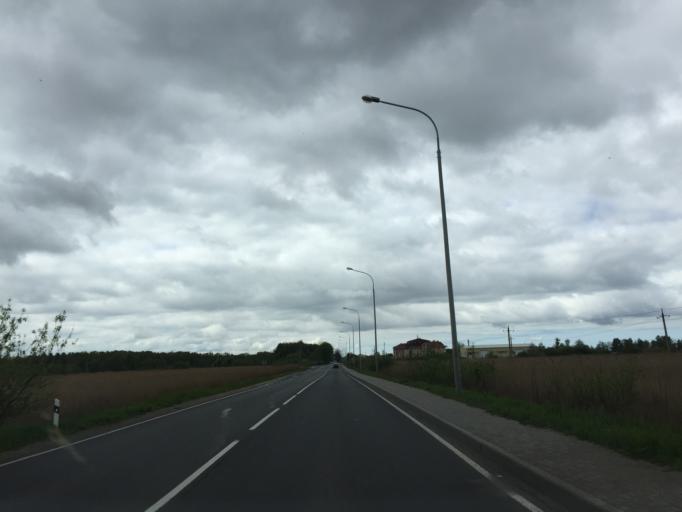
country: RU
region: Kaliningrad
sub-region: Gorod Kaliningrad
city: Kaliningrad
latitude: 54.6613
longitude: 20.4043
